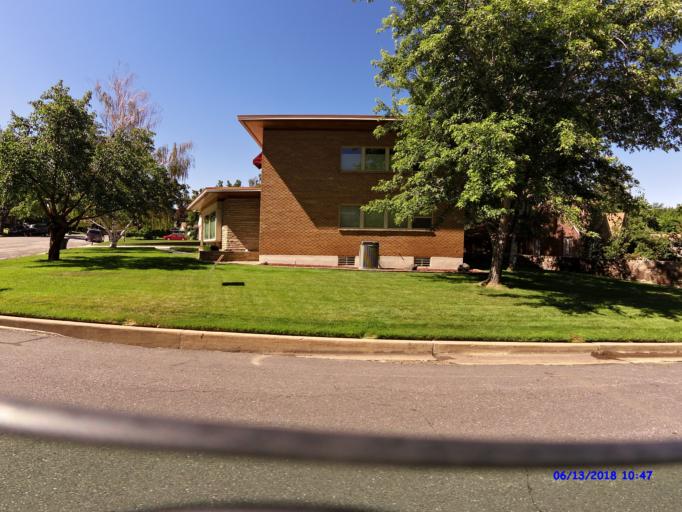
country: US
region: Utah
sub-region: Weber County
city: Ogden
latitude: 41.2139
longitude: -111.9384
